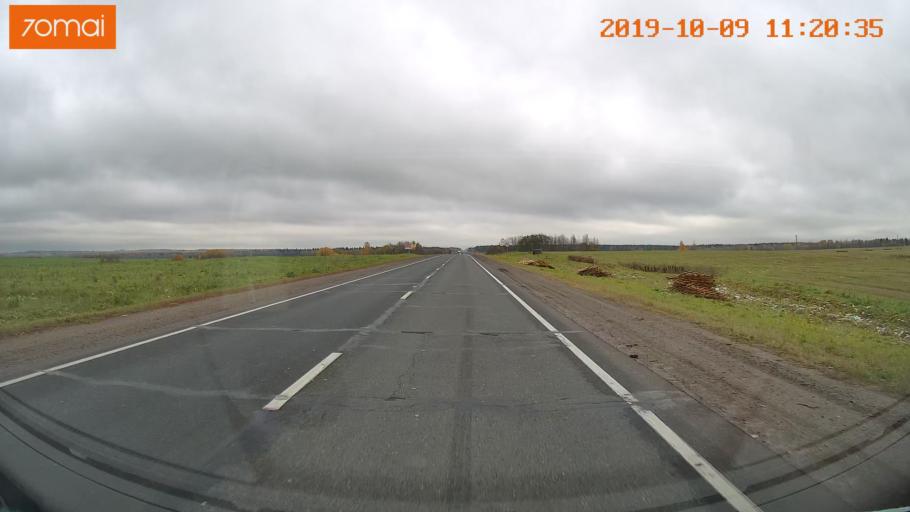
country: RU
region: Vologda
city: Vologda
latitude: 59.1480
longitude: 39.9402
